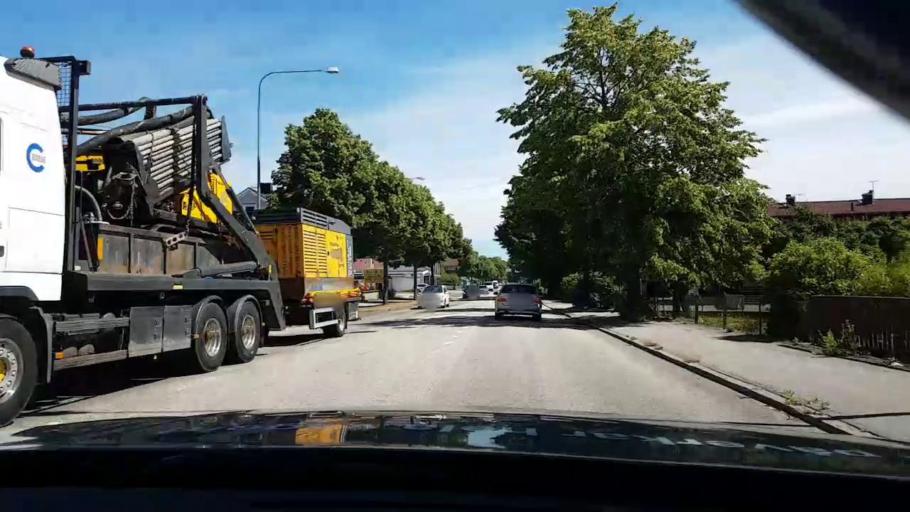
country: SE
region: Kalmar
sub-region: Vasterviks Kommun
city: Vaestervik
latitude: 57.7593
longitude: 16.6168
